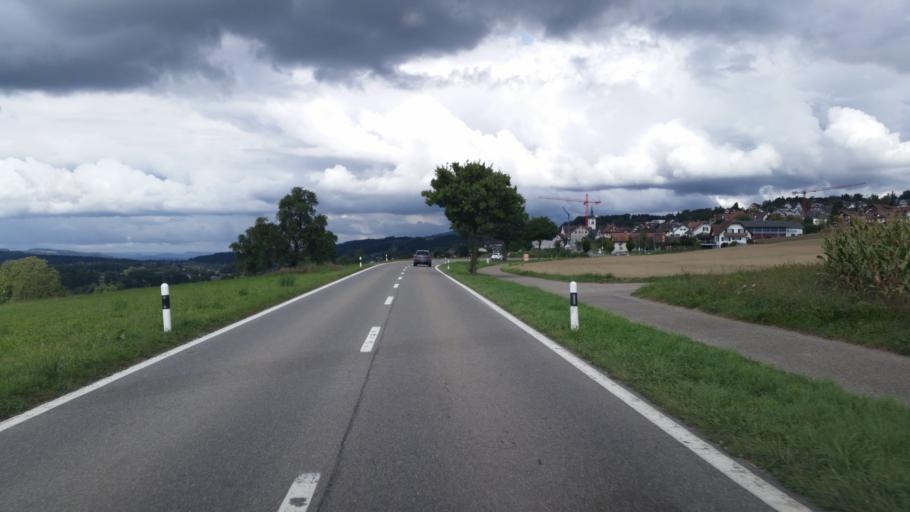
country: CH
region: Aargau
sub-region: Bezirk Bremgarten
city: Oberlunkhofen
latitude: 47.3055
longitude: 8.3907
